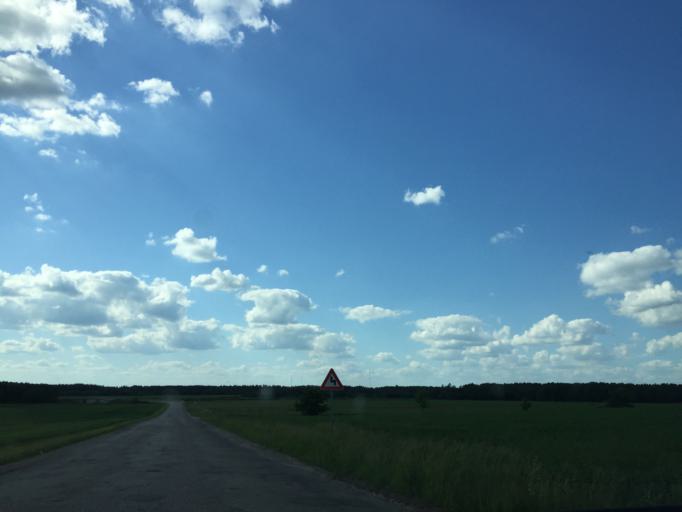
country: LV
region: Jaunpils
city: Jaunpils
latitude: 56.8542
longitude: 23.0271
